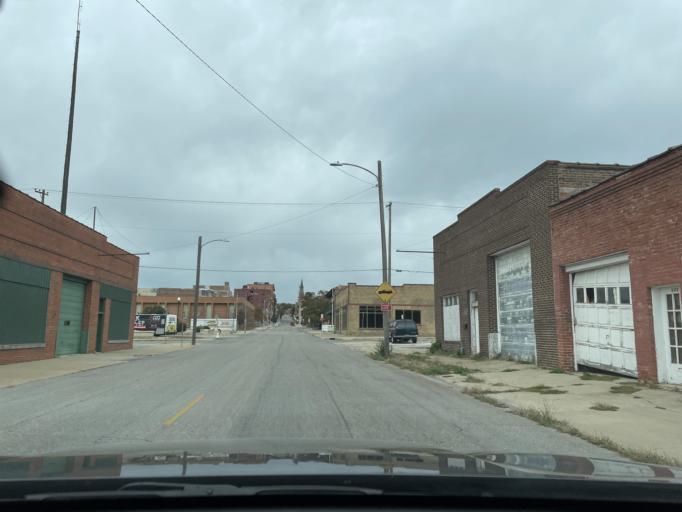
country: US
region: Missouri
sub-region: Buchanan County
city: Saint Joseph
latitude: 39.7629
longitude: -94.8518
